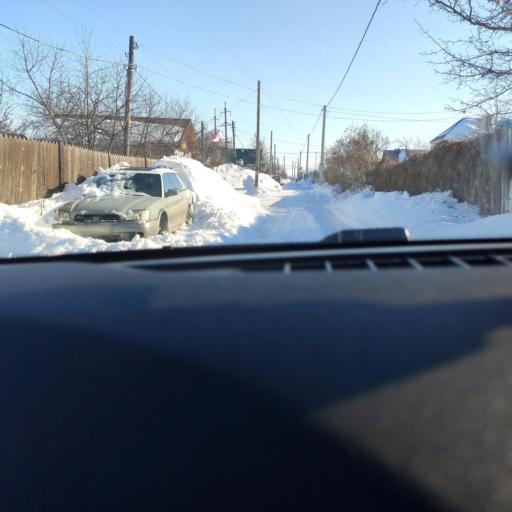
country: RU
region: Samara
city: Petra-Dubrava
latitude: 53.2859
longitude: 50.3076
